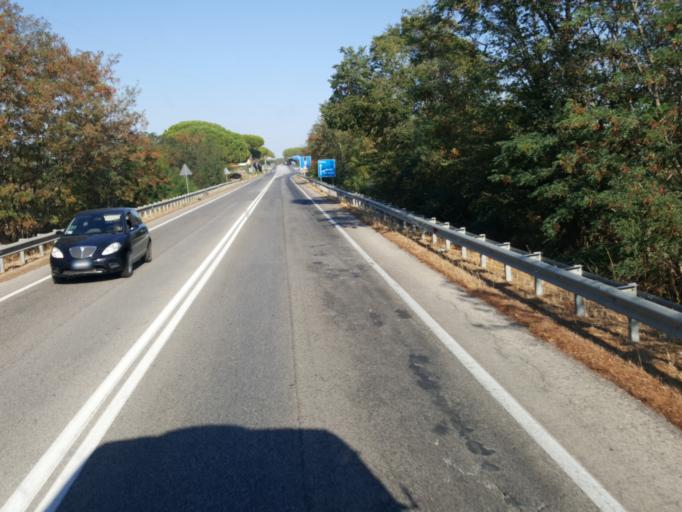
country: IT
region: Latium
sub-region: Provincia di Viterbo
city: Pescia Romana
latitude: 42.4143
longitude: 11.4570
